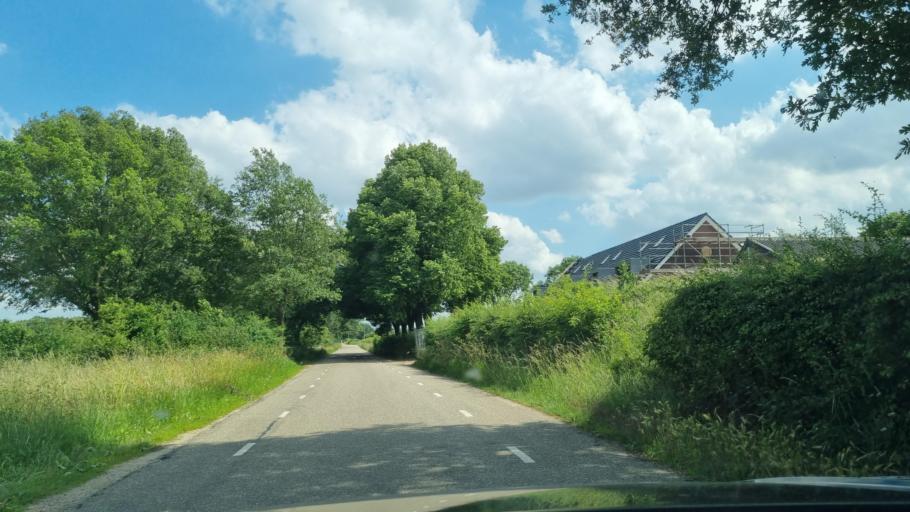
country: NL
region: North Brabant
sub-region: Gemeente Cuijk
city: Cuijk
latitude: 51.7391
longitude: 5.8973
